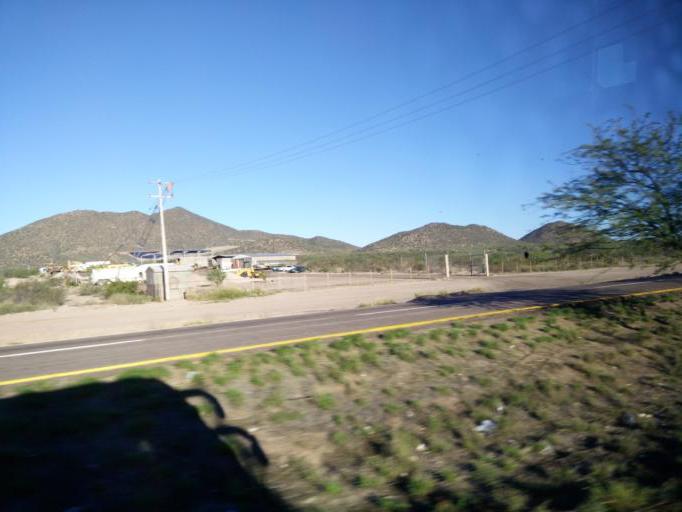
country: MX
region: Sonora
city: Heroica Guaymas
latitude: 27.9968
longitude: -110.9385
